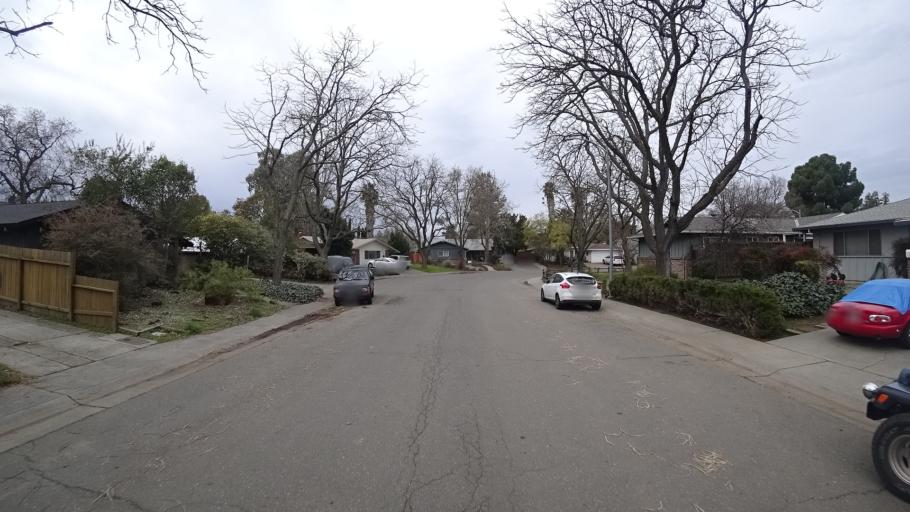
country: US
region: California
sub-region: Yolo County
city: Davis
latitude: 38.5568
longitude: -121.7259
